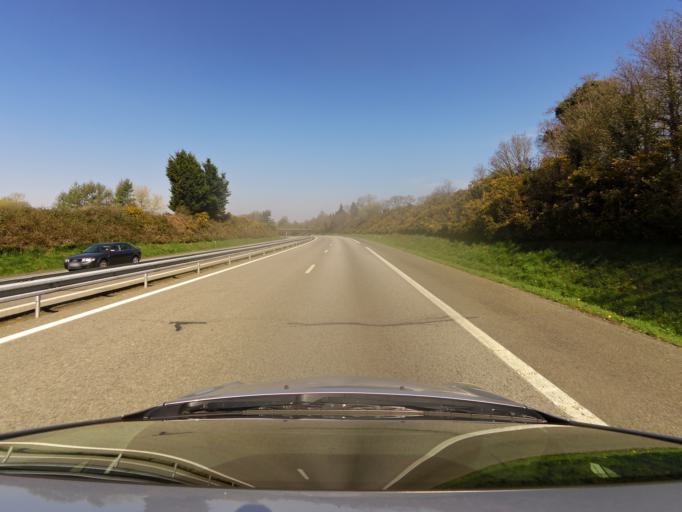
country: FR
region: Brittany
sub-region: Departement du Morbihan
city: Ploermel
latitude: 47.9279
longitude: -2.4155
